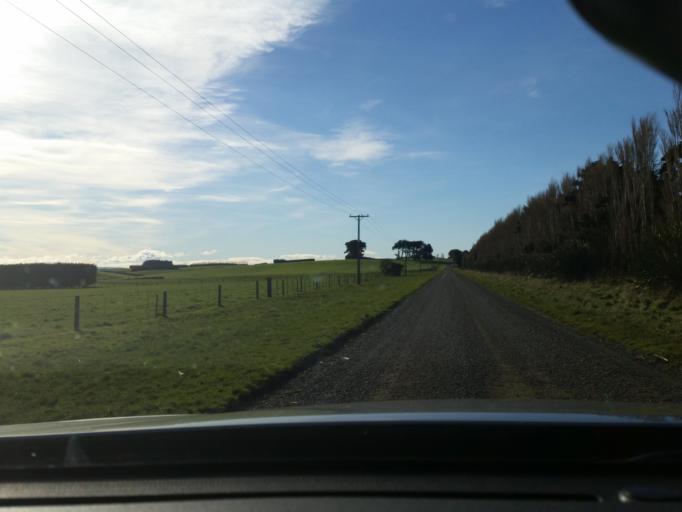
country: NZ
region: Southland
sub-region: Southland District
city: Riverton
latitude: -46.2945
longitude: 168.0418
